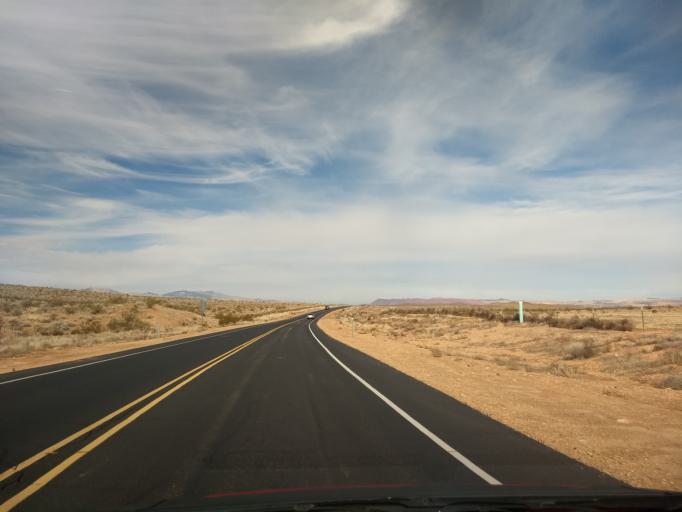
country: US
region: Utah
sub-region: Washington County
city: Washington
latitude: 37.0159
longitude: -113.4966
